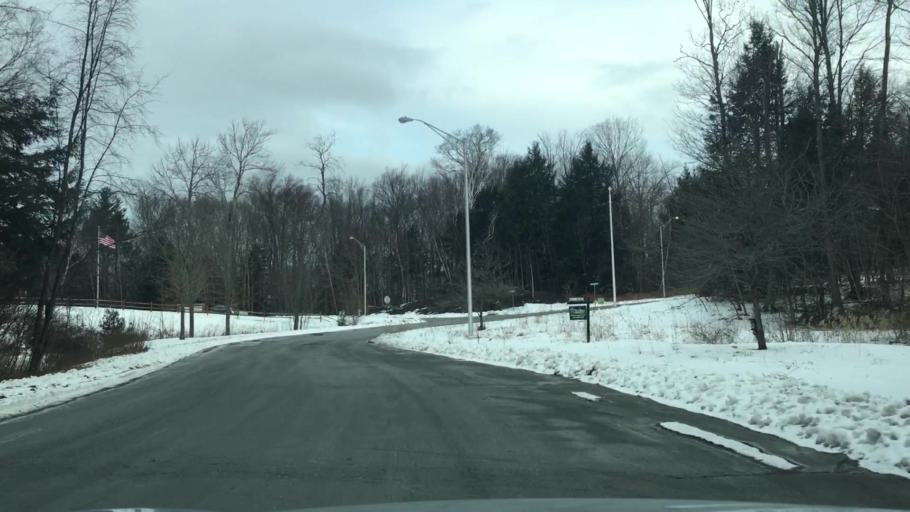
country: US
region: Massachusetts
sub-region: Berkshire County
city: Pittsfield
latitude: 42.4128
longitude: -73.2692
